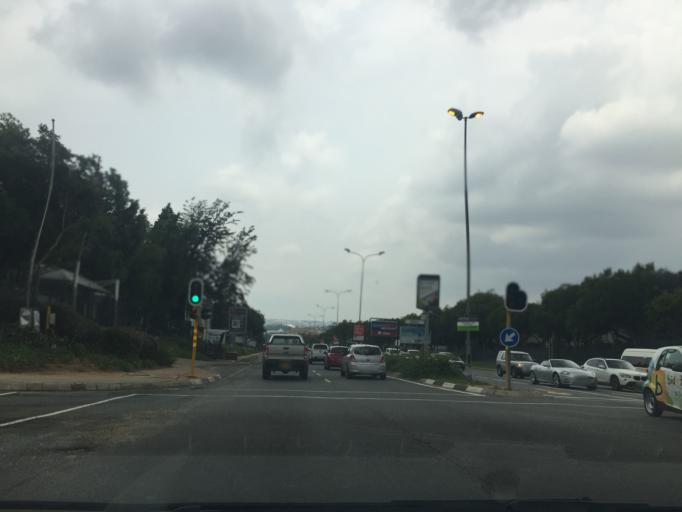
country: ZA
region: Gauteng
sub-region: City of Johannesburg Metropolitan Municipality
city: Midrand
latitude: -26.0438
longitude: 28.0598
